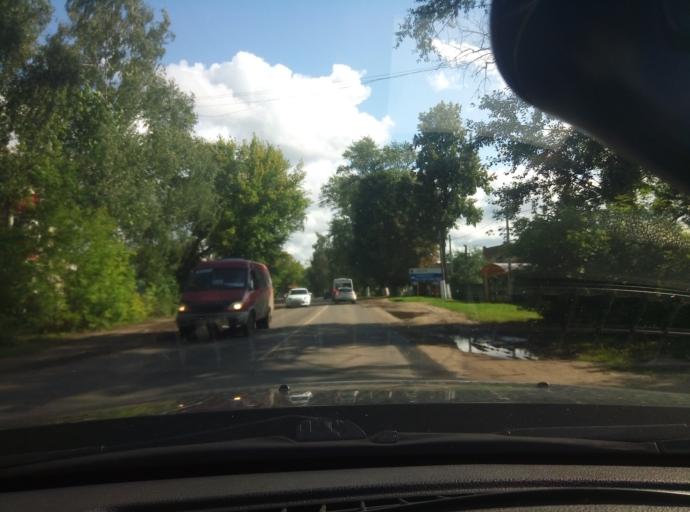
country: RU
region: Tula
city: Donskoy
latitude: 53.9770
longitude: 38.3097
